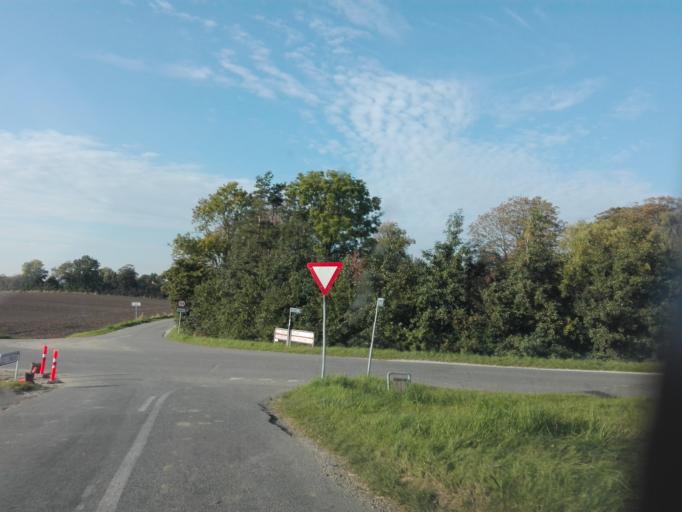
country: DK
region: Central Jutland
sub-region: Odder Kommune
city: Odder
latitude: 55.9929
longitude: 10.1910
